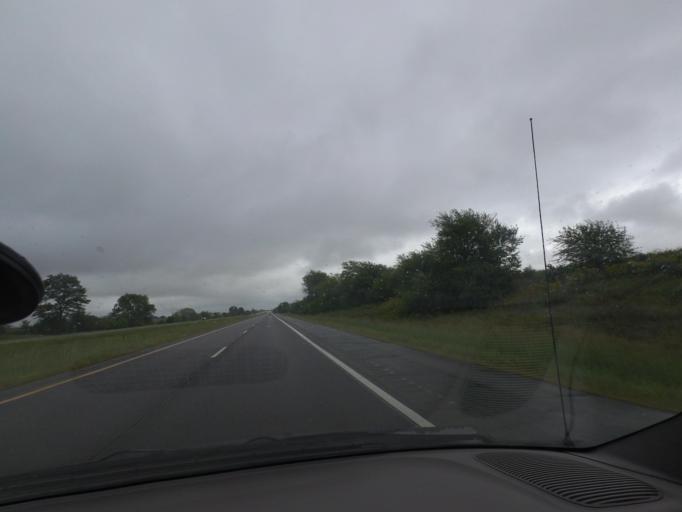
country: US
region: Illinois
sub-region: Champaign County
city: Mahomet
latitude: 40.1203
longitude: -88.4378
